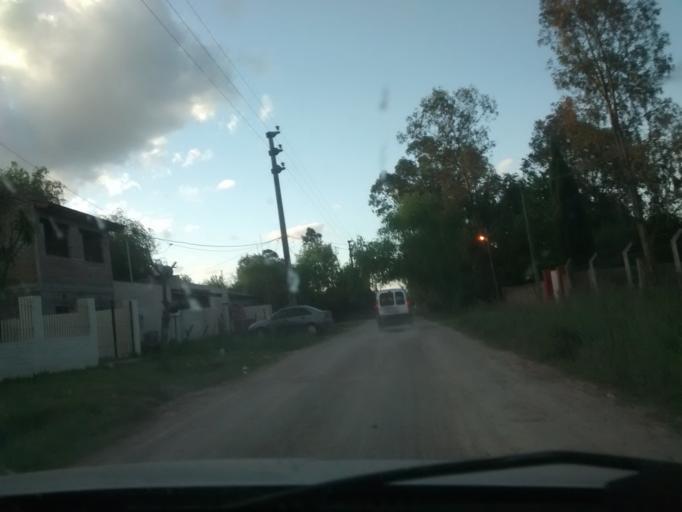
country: AR
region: Buenos Aires
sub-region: Partido de Brandsen
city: Brandsen
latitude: -35.1715
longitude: -58.2208
